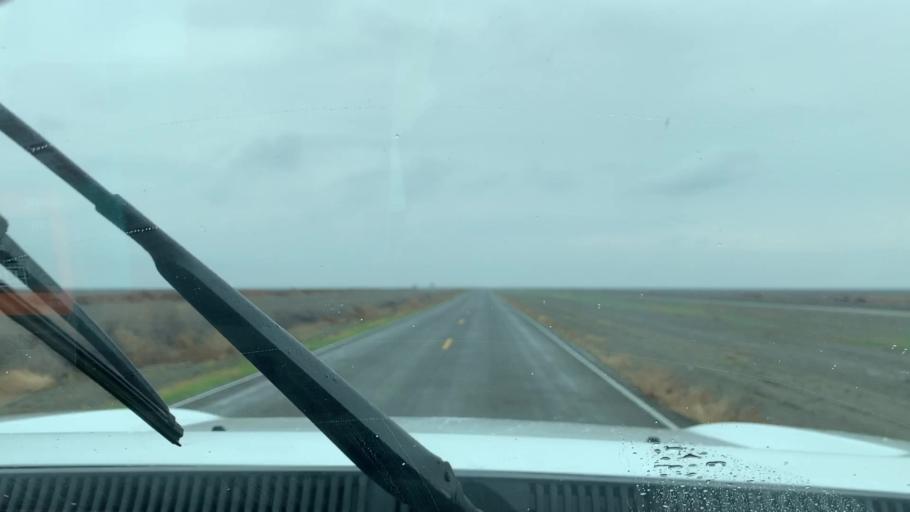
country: US
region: California
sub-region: Tulare County
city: Alpaugh
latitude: 35.9340
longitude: -119.6660
